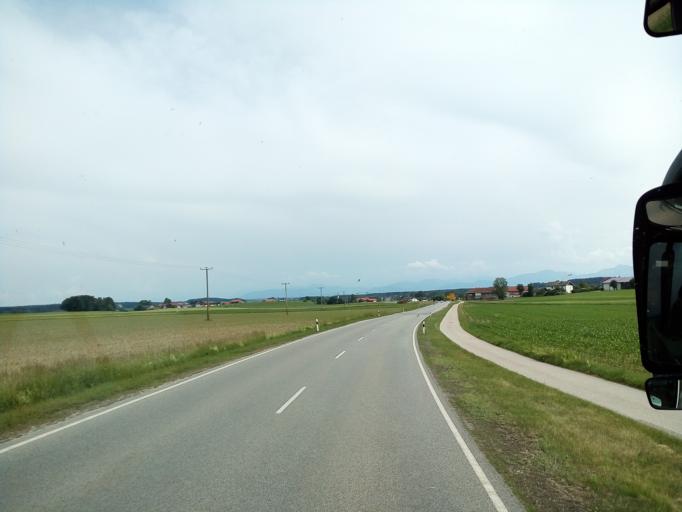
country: DE
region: Bavaria
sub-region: Upper Bavaria
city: Obing
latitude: 48.0198
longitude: 12.3803
